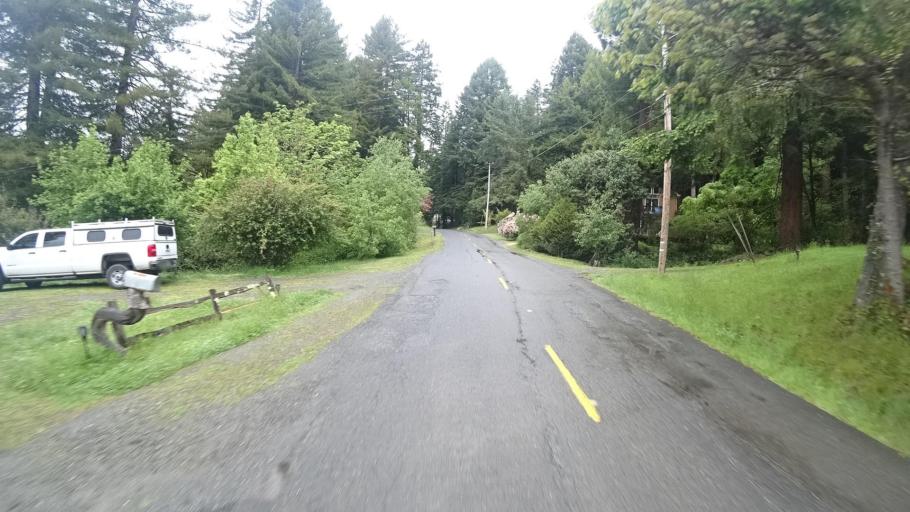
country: US
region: California
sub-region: Humboldt County
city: Bayside
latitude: 40.8229
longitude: -124.0335
